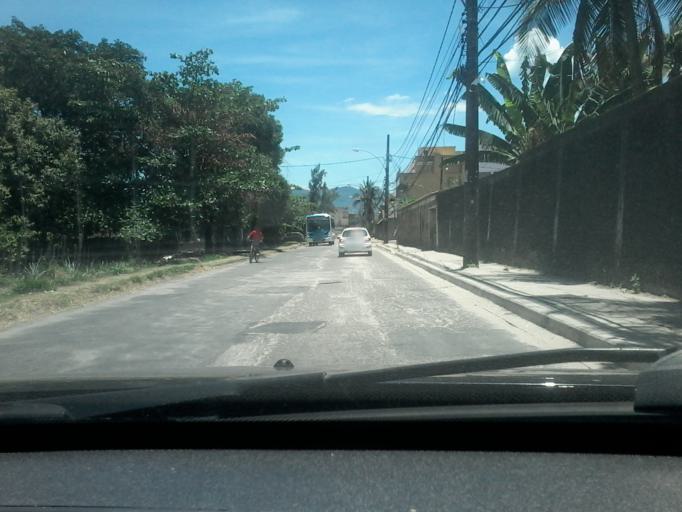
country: BR
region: Rio de Janeiro
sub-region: Nilopolis
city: Nilopolis
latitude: -23.0287
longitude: -43.4804
